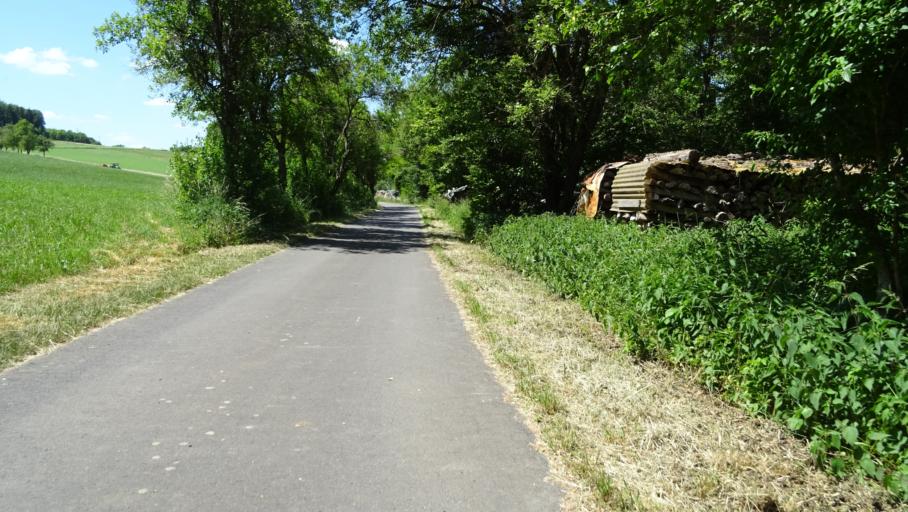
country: DE
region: Baden-Wuerttemberg
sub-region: Karlsruhe Region
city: Seckach
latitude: 49.4361
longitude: 9.3510
